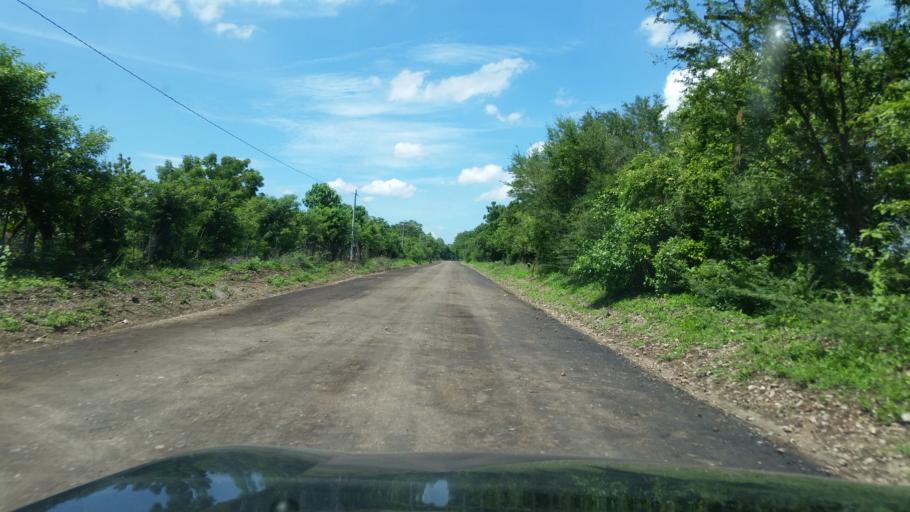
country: NI
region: Chinandega
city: El Viejo
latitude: 12.7502
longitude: -87.1339
